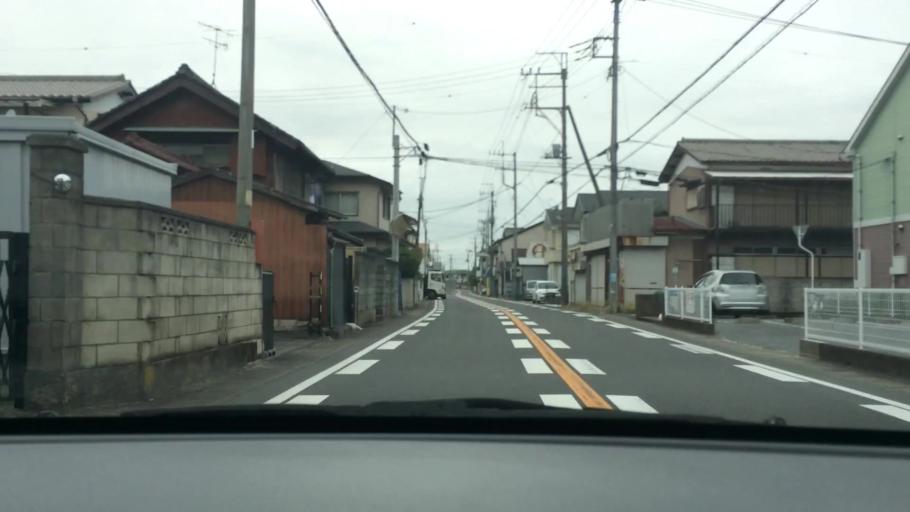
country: JP
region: Chiba
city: Nagareyama
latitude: 35.8595
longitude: 139.9009
